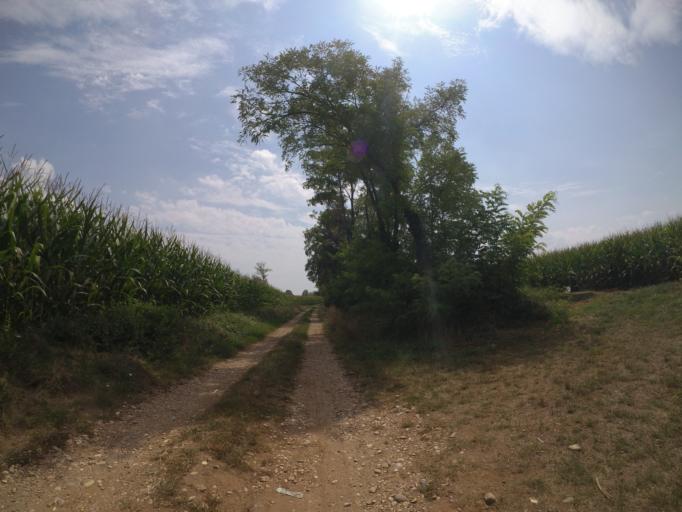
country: IT
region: Friuli Venezia Giulia
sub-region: Provincia di Udine
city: Bertiolo
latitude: 45.9610
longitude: 13.0689
